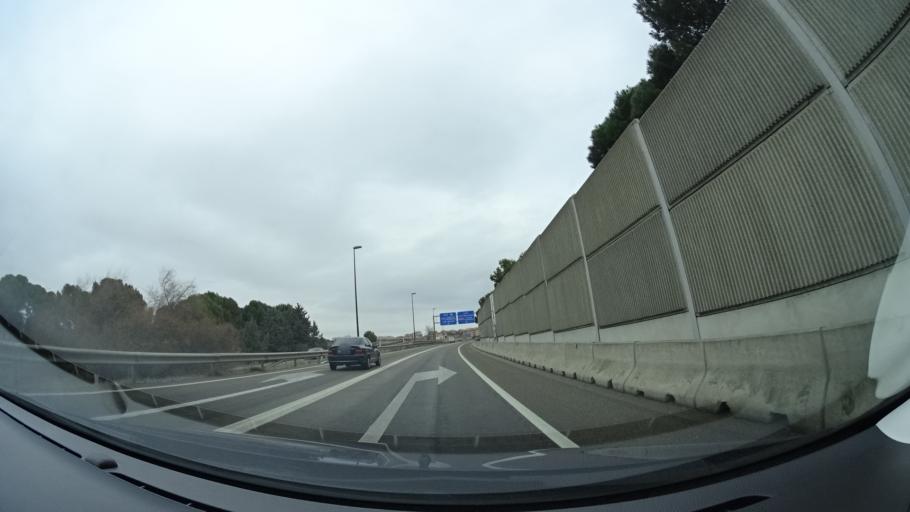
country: ES
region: Aragon
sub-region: Provincia de Zaragoza
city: Zaragoza
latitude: 41.6781
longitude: -0.8775
